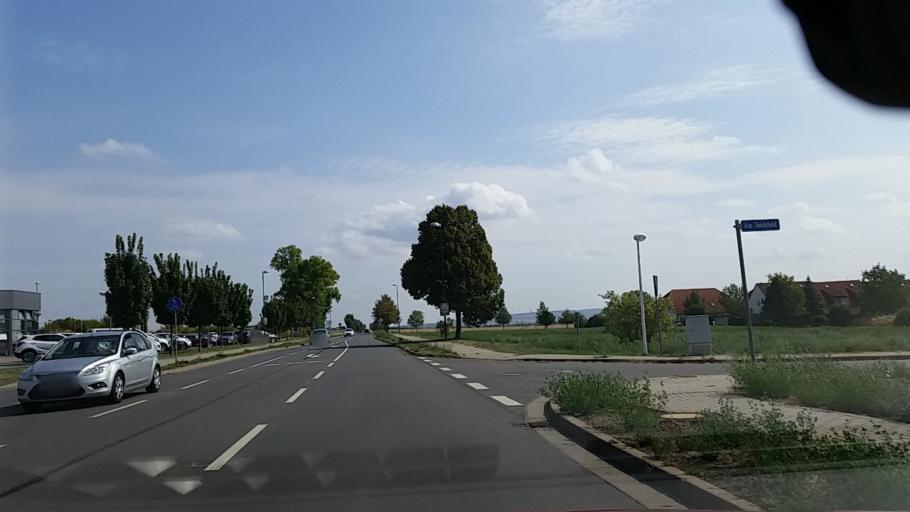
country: DE
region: Thuringia
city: Bad Frankenhausen
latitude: 51.3546
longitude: 11.1150
